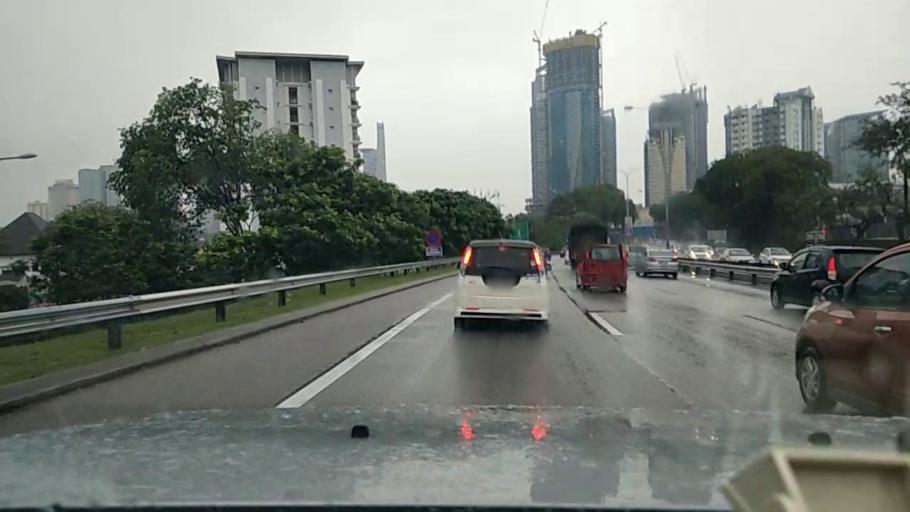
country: MY
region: Kuala Lumpur
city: Kuala Lumpur
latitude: 3.1127
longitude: 101.6822
